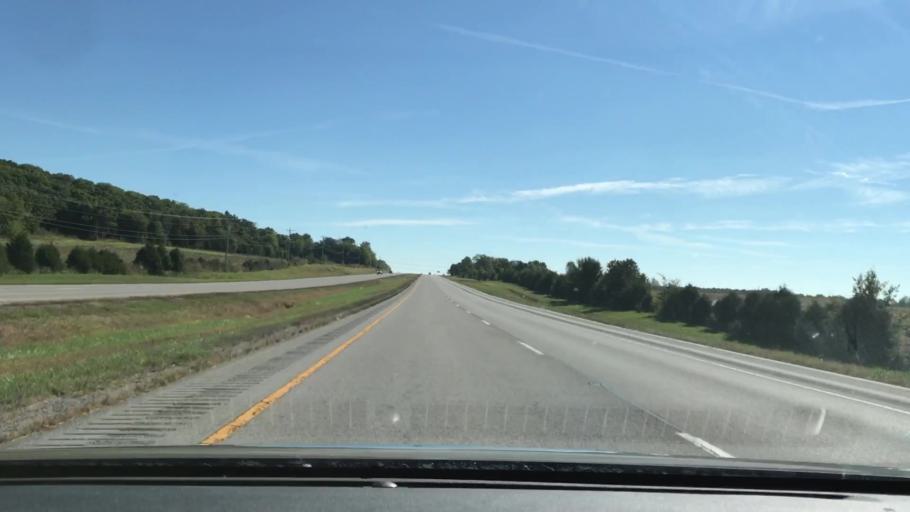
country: US
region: Kentucky
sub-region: Todd County
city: Elkton
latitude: 36.8250
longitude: -87.2116
